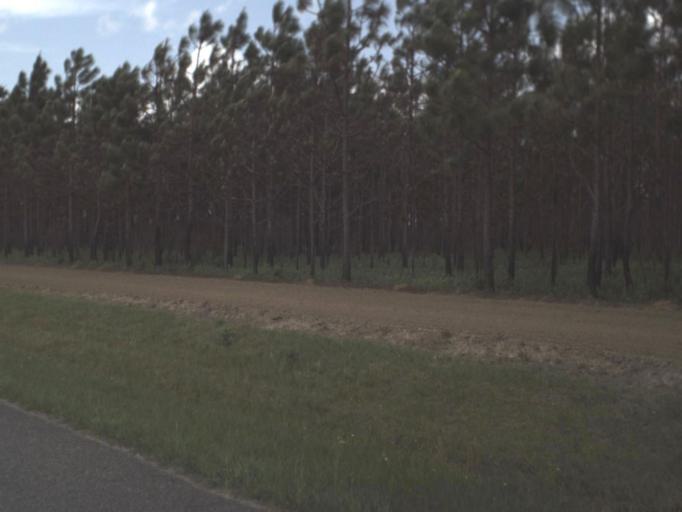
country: US
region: Florida
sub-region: Santa Rosa County
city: Point Baker
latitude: 30.8068
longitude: -87.1197
